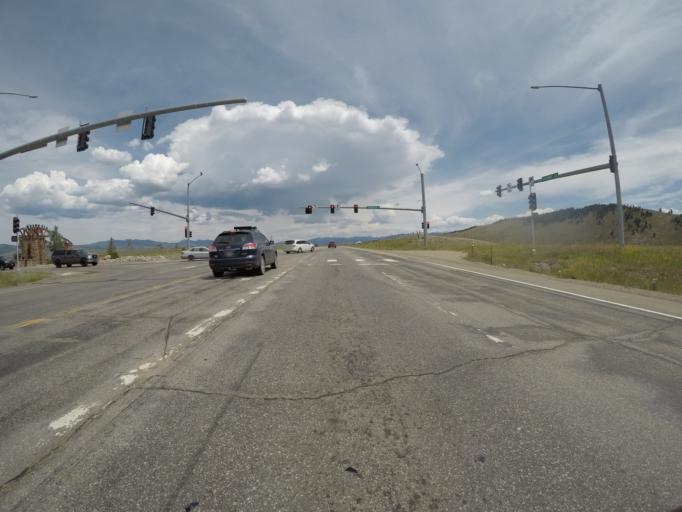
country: US
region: Colorado
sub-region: Grand County
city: Granby
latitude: 40.0629
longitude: -105.9262
